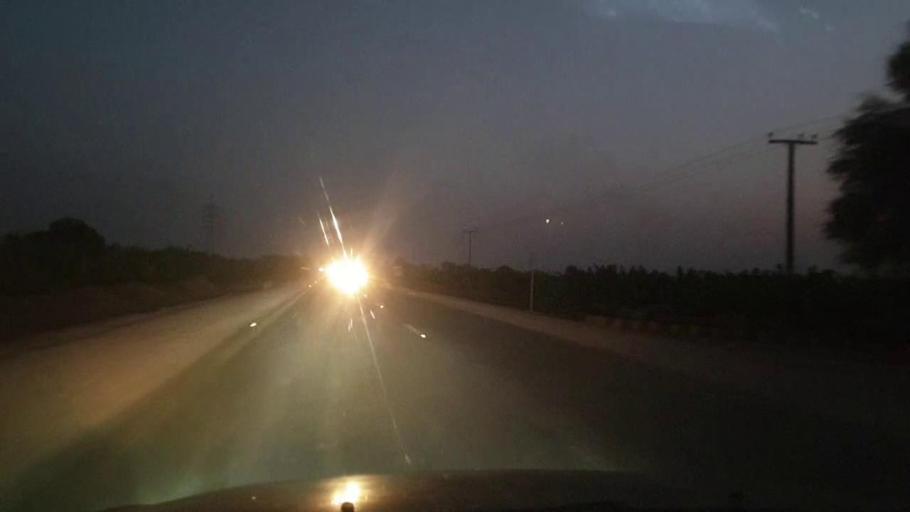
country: PK
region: Sindh
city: Chambar
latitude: 25.3615
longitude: 68.7857
